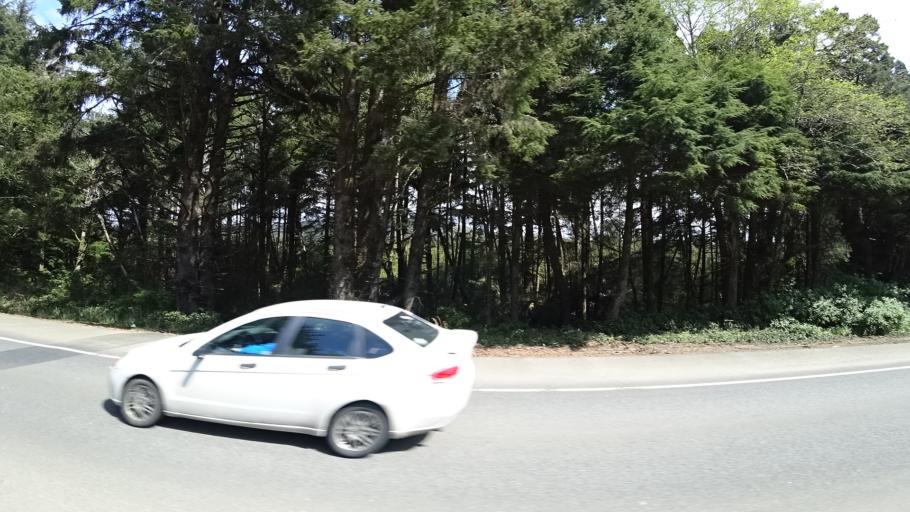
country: US
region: Oregon
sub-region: Lincoln County
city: Lincoln Beach
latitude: 44.8728
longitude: -124.0342
